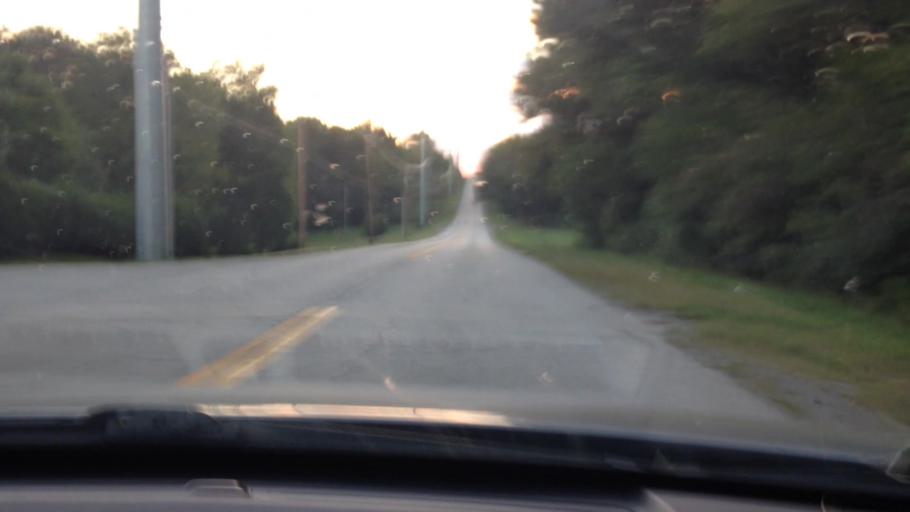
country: US
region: Kansas
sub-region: Leavenworth County
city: Lansing
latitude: 39.1866
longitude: -94.8083
